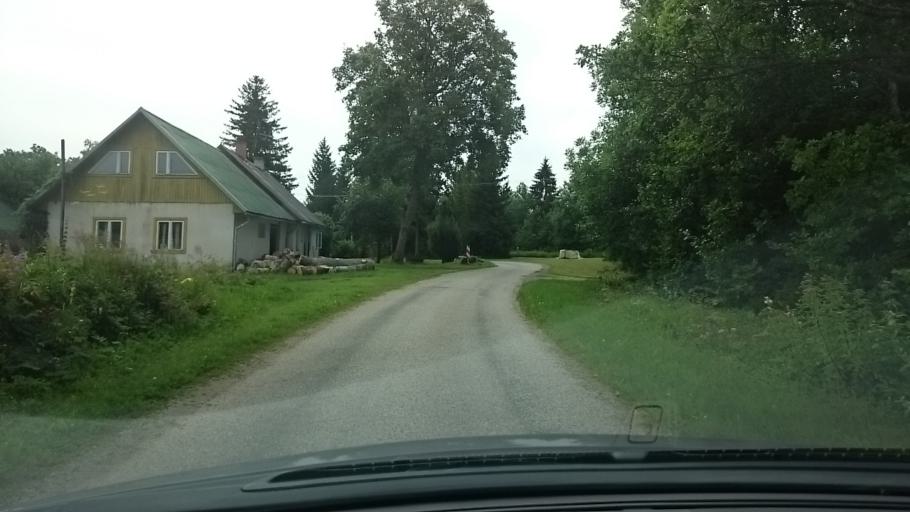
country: EE
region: Laeaene
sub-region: Ridala Parish
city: Uuemoisa
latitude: 58.9788
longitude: 23.6788
